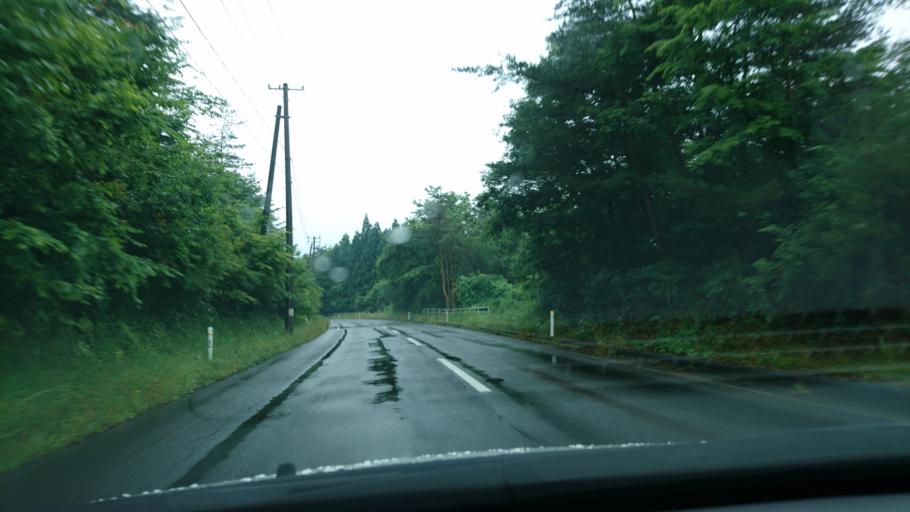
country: JP
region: Iwate
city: Ichinoseki
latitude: 38.9359
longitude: 141.0513
